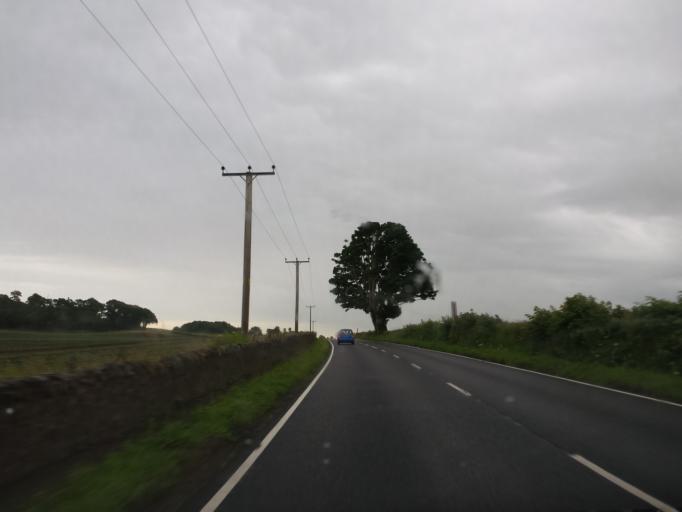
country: GB
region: Scotland
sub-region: Fife
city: Newport-On-Tay
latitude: 56.4280
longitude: -2.9308
